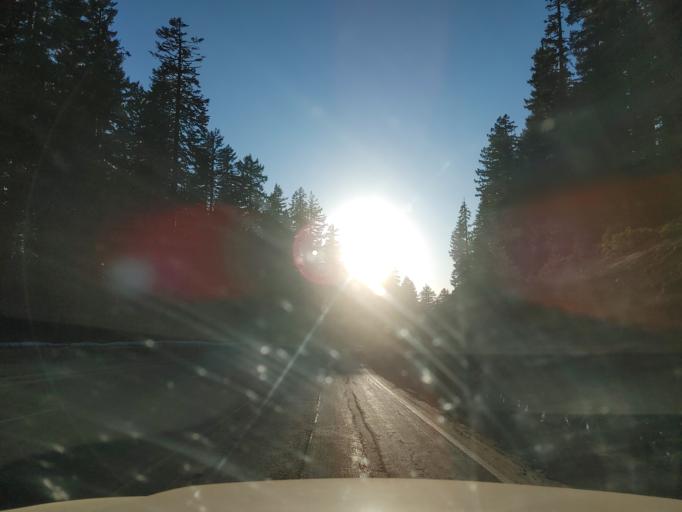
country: US
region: Oregon
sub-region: Lane County
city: Oakridge
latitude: 43.6118
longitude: -122.0627
